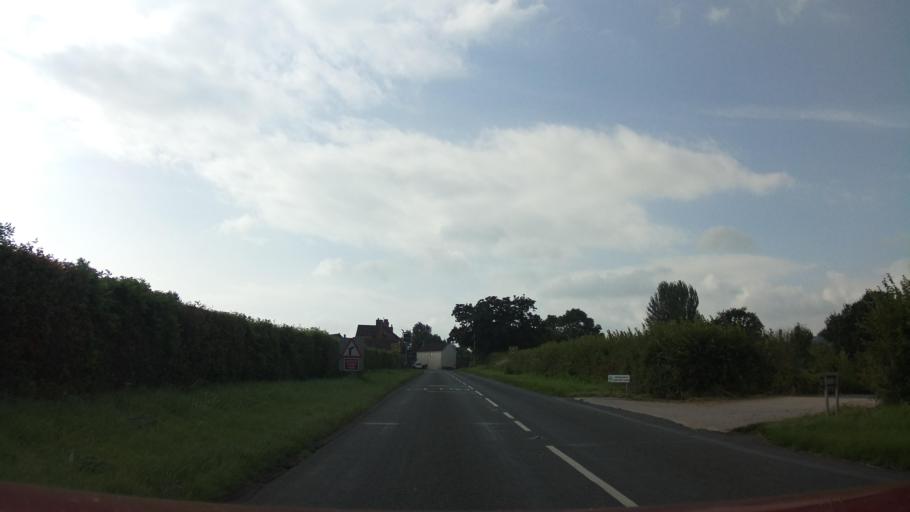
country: GB
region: England
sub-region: Bath and North East Somerset
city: Compton Martin
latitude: 51.3181
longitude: -2.6379
